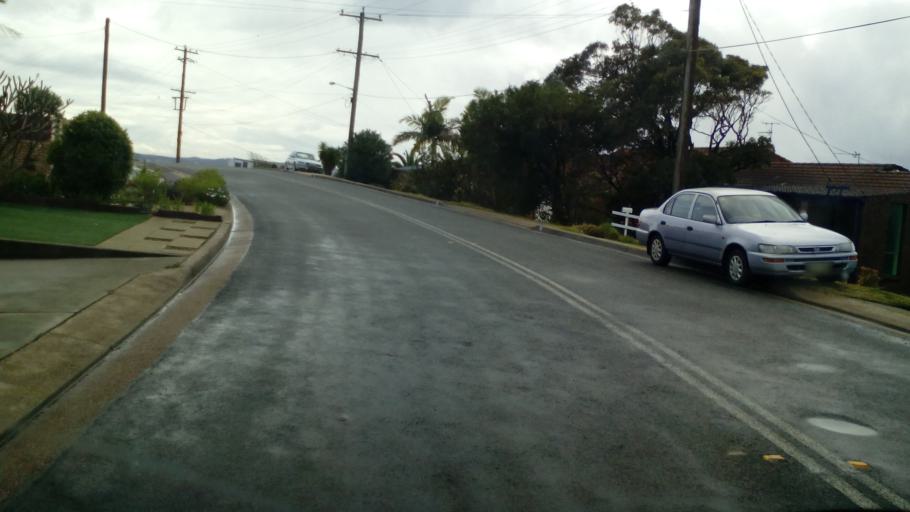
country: AU
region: New South Wales
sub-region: Lake Macquarie Shire
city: Belmont South
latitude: -33.1120
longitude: 151.6411
